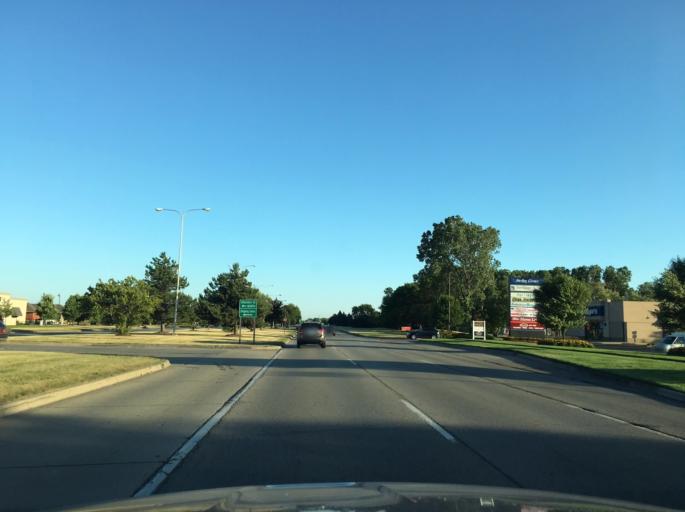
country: US
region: Michigan
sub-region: Macomb County
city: Utica
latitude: 42.6232
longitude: -82.9930
